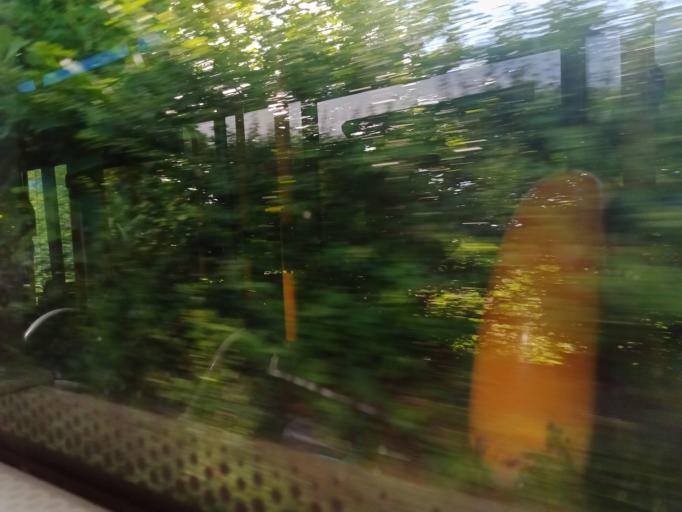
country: GB
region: Wales
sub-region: Anglesey
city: Llangoed
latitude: 53.2978
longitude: -4.0834
